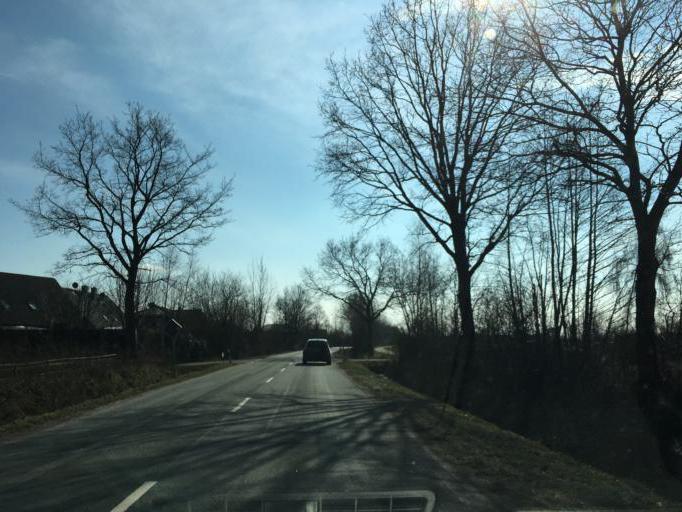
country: DE
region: Schleswig-Holstein
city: Escheburg
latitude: 53.4754
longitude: 10.3138
